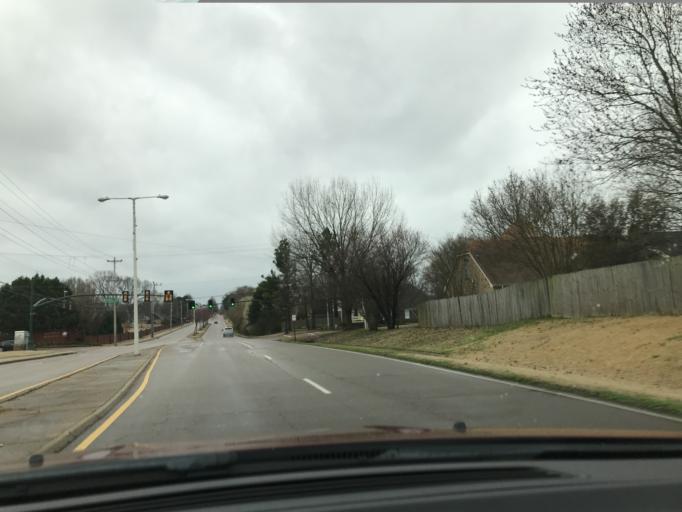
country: US
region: Tennessee
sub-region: Shelby County
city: Collierville
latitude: 35.0622
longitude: -89.6860
